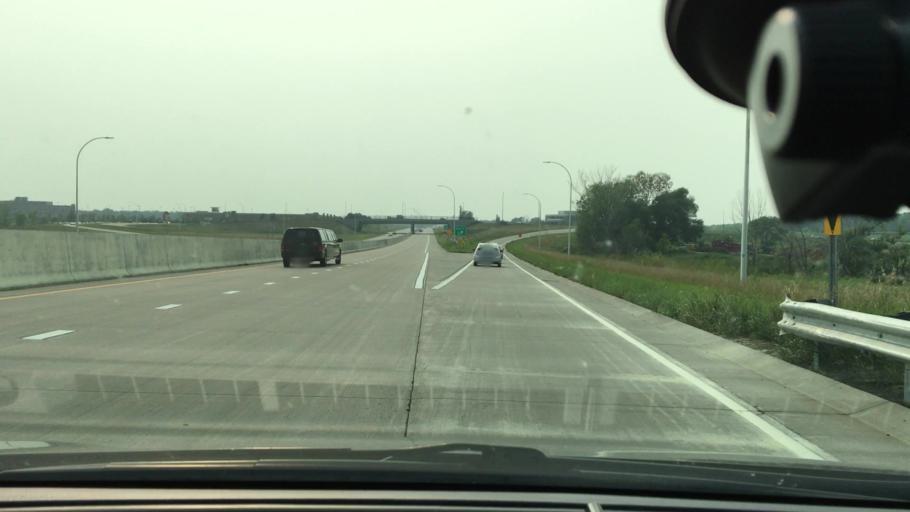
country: US
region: Minnesota
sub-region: Hennepin County
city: Maple Grove
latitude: 45.1377
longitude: -93.4661
